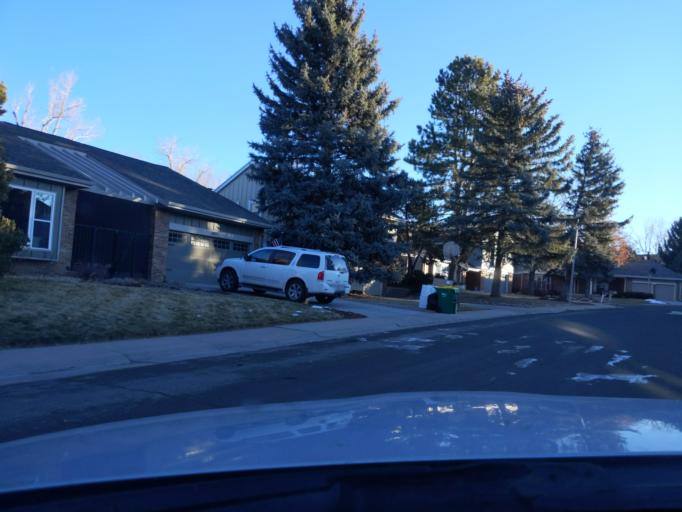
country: US
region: Colorado
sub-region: Arapahoe County
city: Centennial
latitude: 39.5710
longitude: -104.8872
